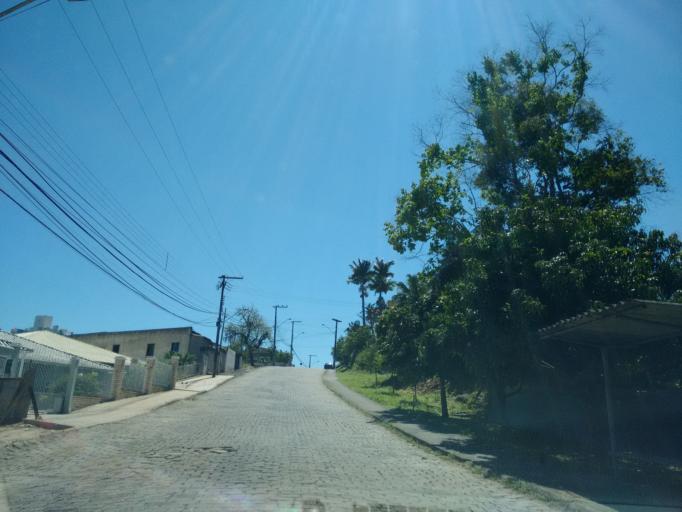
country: BR
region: Santa Catarina
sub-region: Blumenau
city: Blumenau
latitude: -26.8935
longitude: -49.1029
